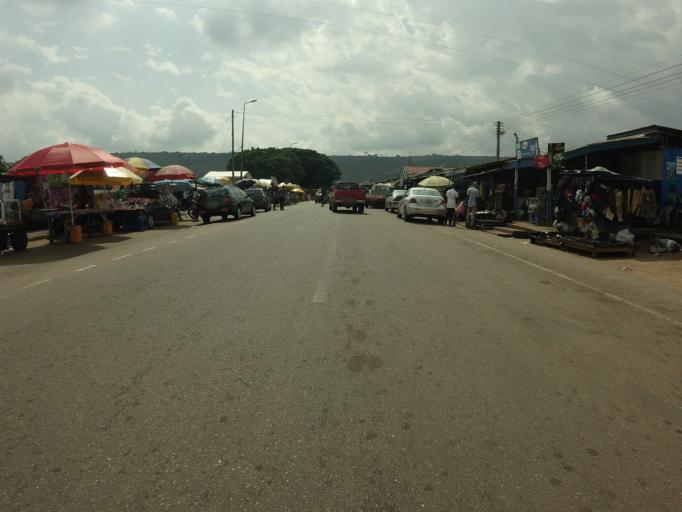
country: GH
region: Volta
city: Ho
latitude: 6.6183
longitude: 0.4719
